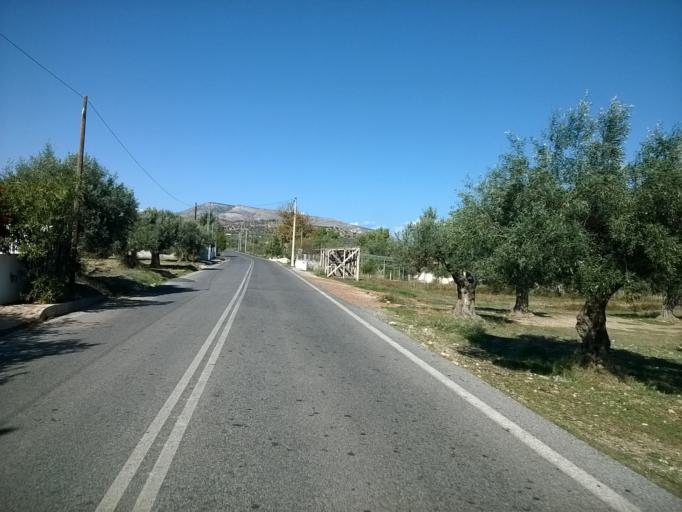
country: GR
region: Attica
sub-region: Nomarchia Anatolikis Attikis
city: Keratea
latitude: 37.7967
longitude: 23.9975
